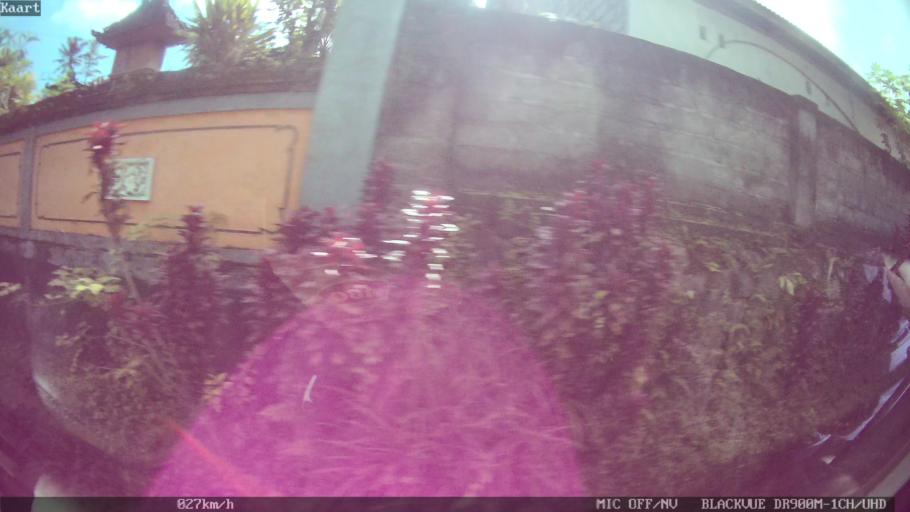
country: ID
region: Bali
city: Banjar Pesalakan
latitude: -8.5093
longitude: 115.3016
